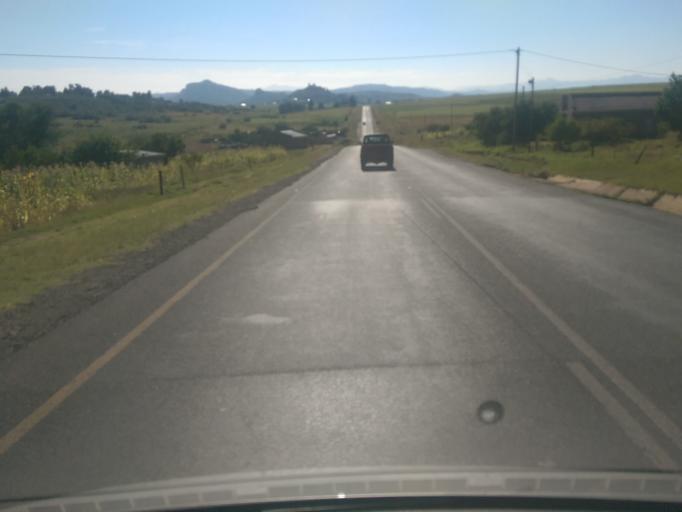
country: LS
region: Maseru
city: Maseru
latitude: -29.4084
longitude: 27.5939
